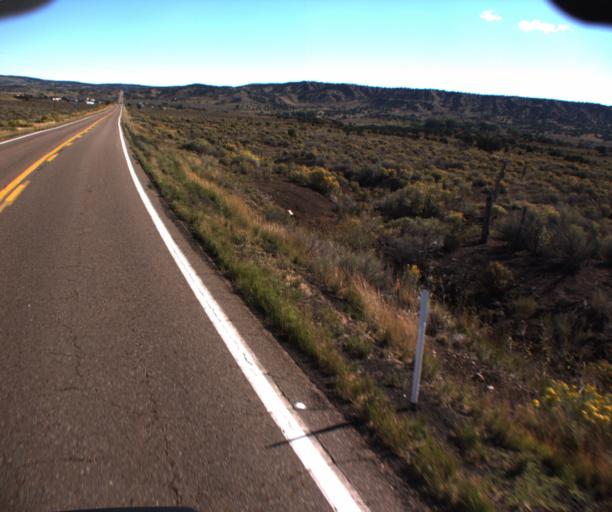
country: US
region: Arizona
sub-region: Apache County
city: Saint Johns
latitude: 34.4677
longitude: -109.6168
